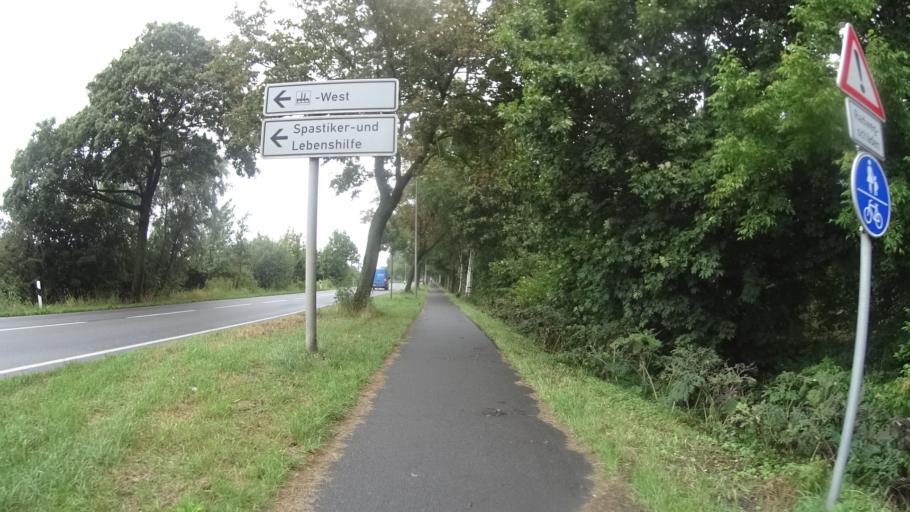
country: DE
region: Lower Saxony
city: Leer
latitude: 53.2196
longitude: 7.4363
